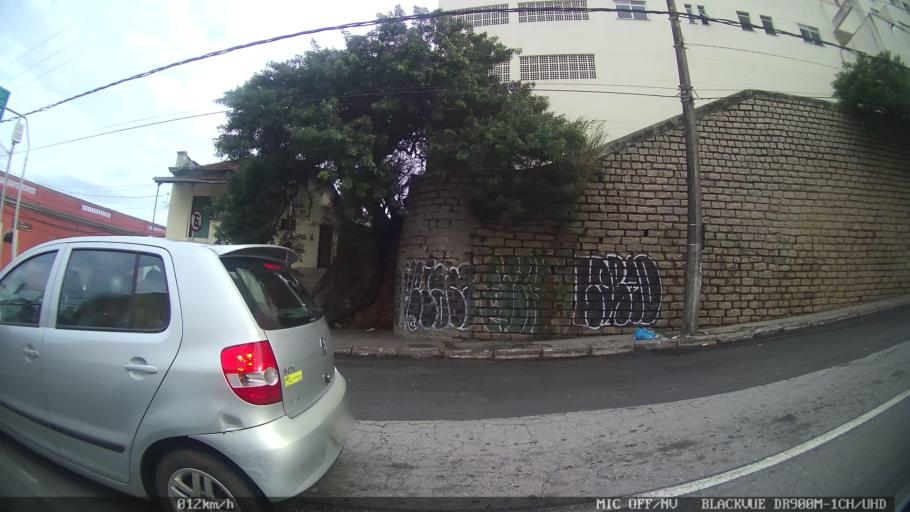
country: BR
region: Santa Catarina
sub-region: Florianopolis
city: Florianopolis
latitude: -27.5952
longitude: -48.5571
